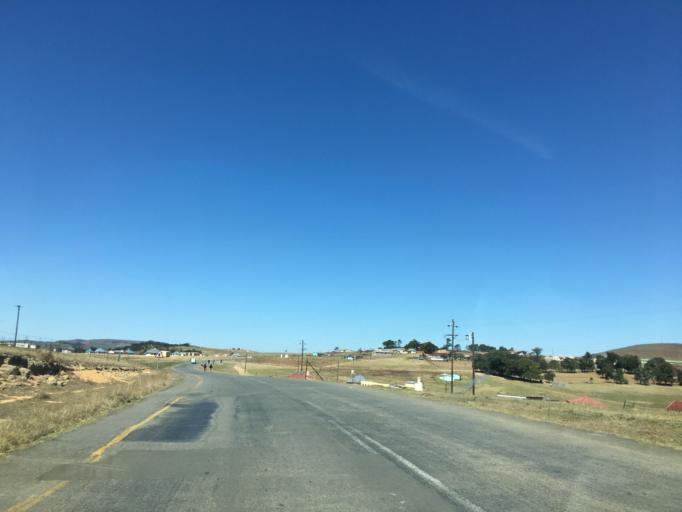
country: ZA
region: Eastern Cape
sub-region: Chris Hani District Municipality
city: Cala
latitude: -31.5546
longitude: 27.8950
